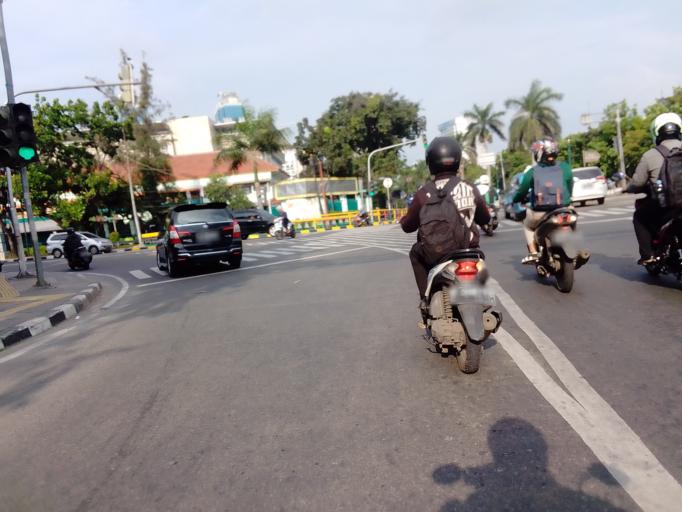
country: ID
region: Jakarta Raya
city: Jakarta
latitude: -6.1818
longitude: 106.8166
